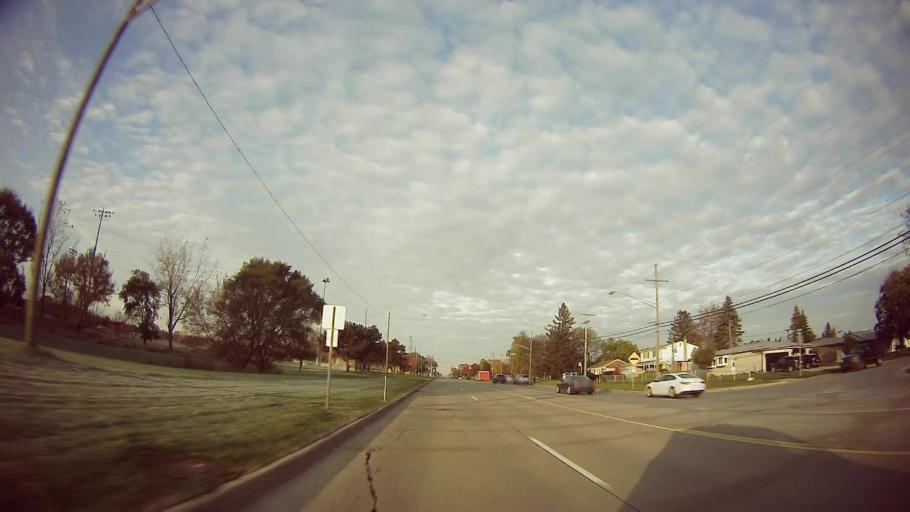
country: US
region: Michigan
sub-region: Macomb County
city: Sterling Heights
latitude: 42.5520
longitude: -82.9940
